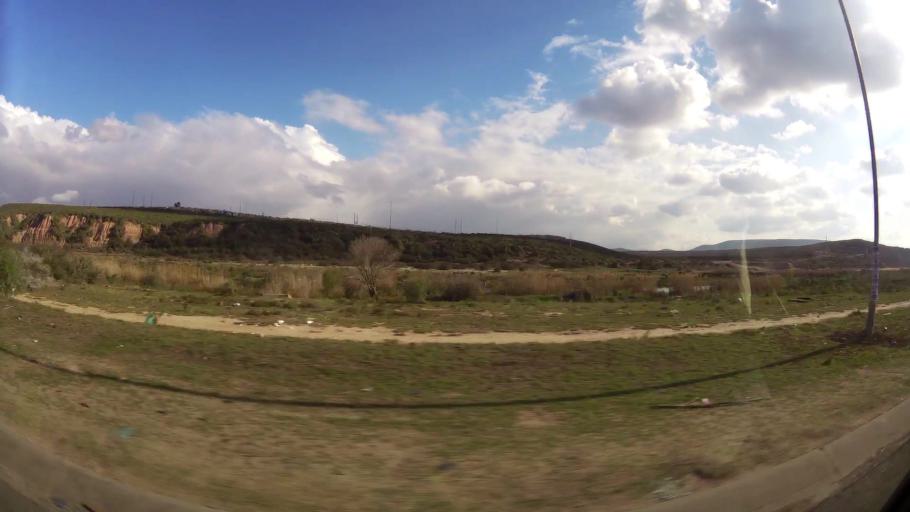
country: ZA
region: Eastern Cape
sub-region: Nelson Mandela Bay Metropolitan Municipality
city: Uitenhage
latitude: -33.7876
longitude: 25.4037
